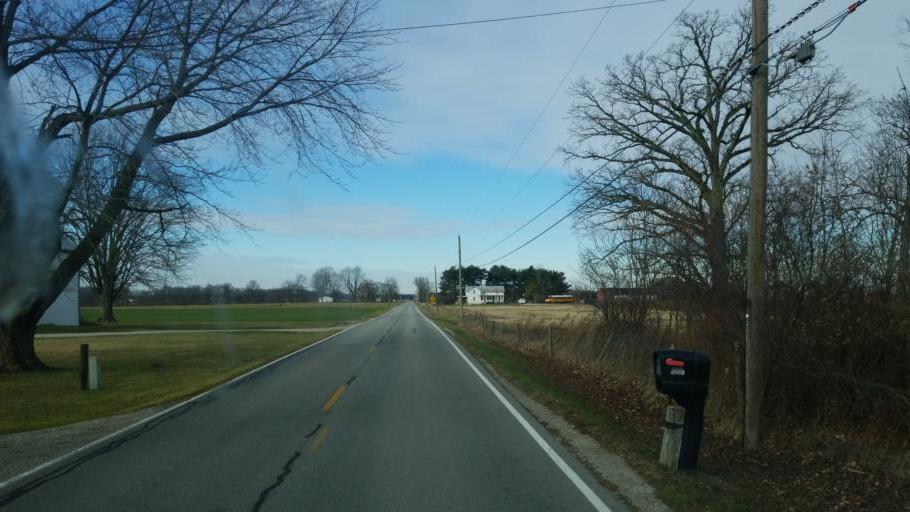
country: US
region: Ohio
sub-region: Marion County
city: Marion
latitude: 40.5642
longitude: -83.0347
